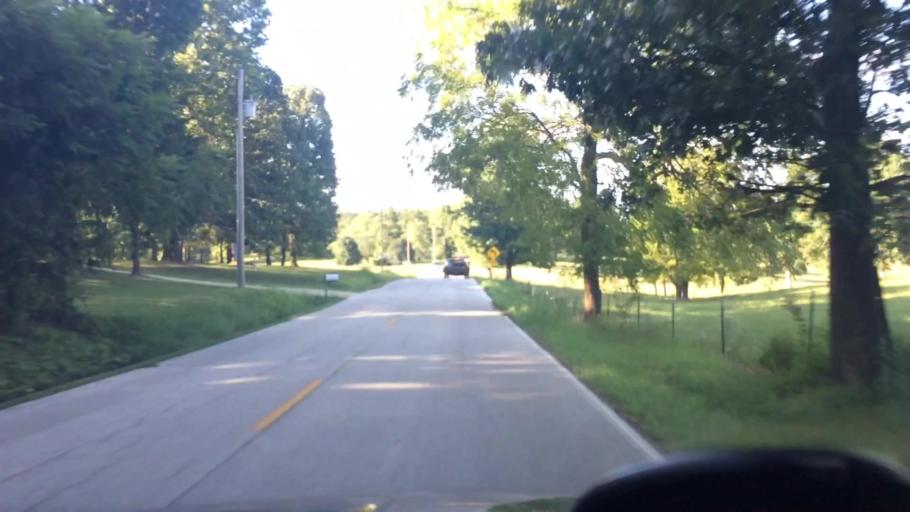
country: US
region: Missouri
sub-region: Greene County
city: Strafford
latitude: 37.2826
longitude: -93.0812
